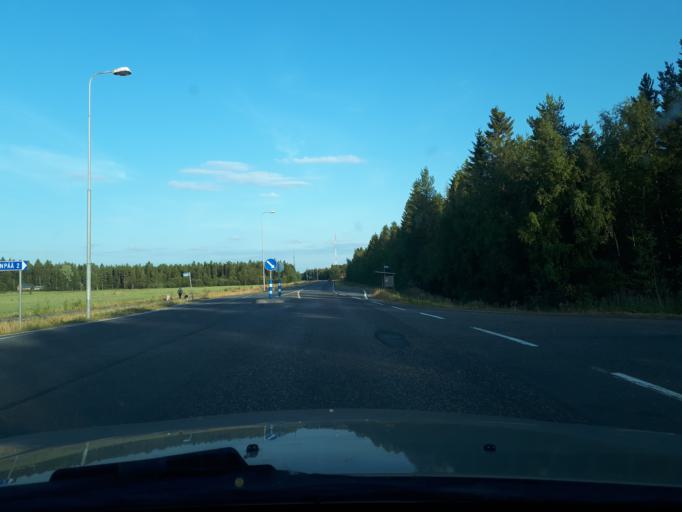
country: FI
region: Northern Ostrobothnia
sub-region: Oulu
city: Oulunsalo
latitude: 64.9790
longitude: 25.2765
